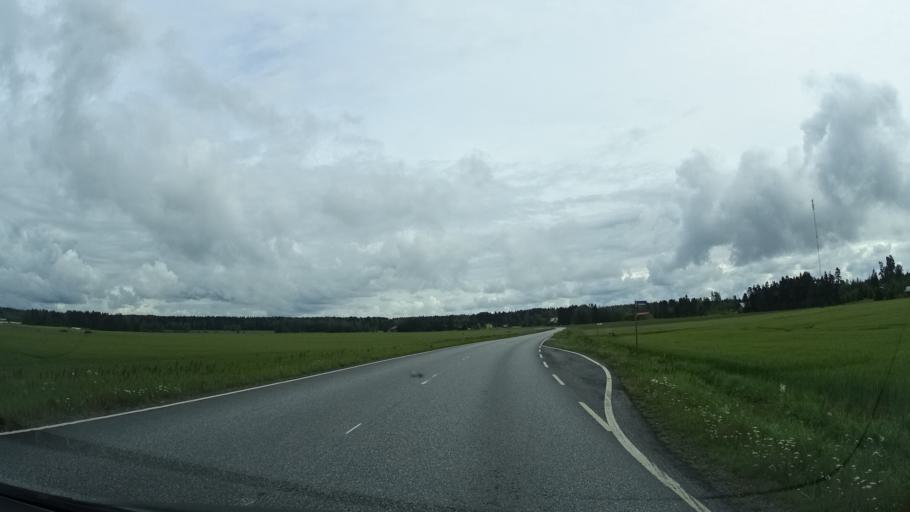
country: FI
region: Haeme
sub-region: Forssa
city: Humppila
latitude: 61.0993
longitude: 23.3050
